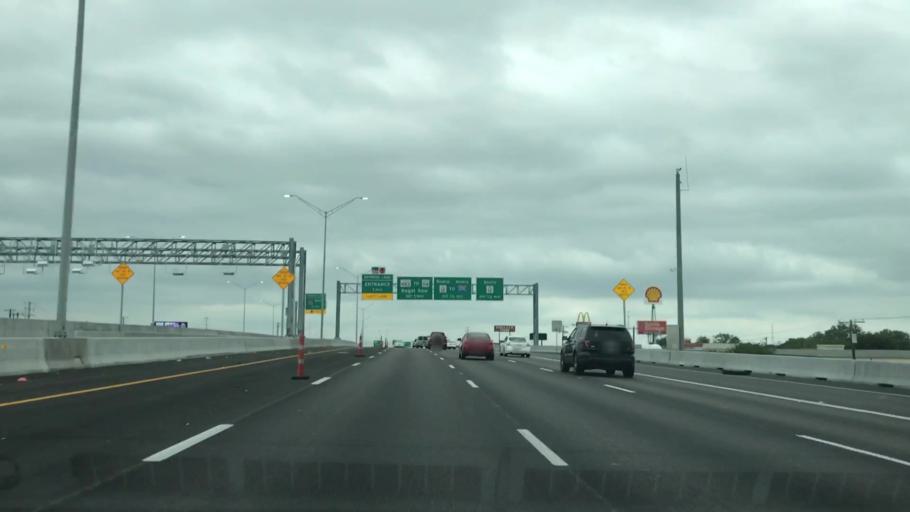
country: US
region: Texas
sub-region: Dallas County
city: Irving
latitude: 32.8369
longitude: -96.9328
